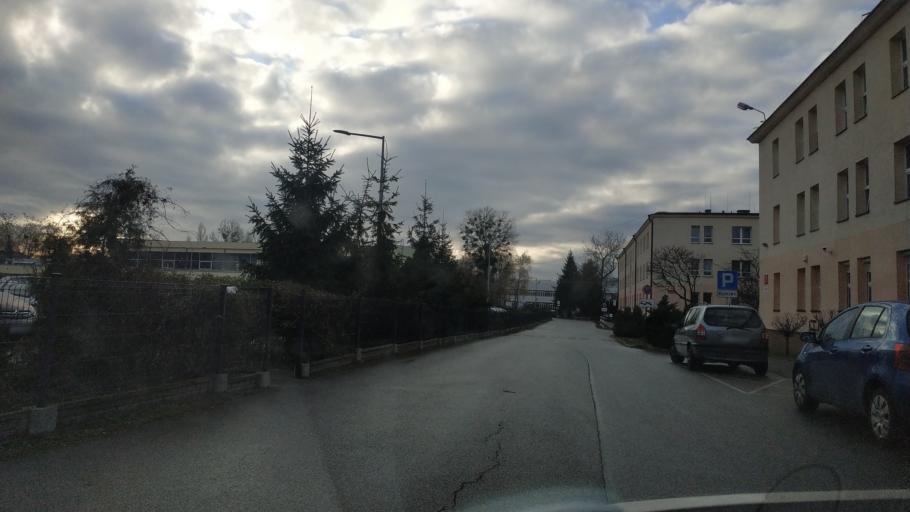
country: PL
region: Kujawsko-Pomorskie
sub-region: Torun
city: Torun
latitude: 53.0240
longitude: 18.5890
